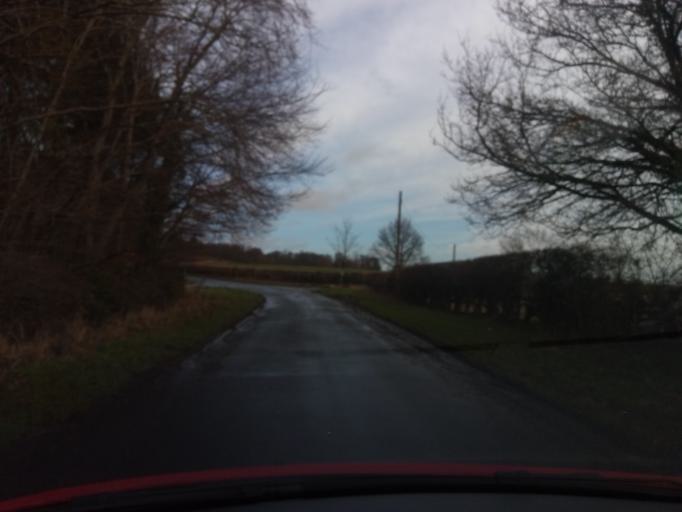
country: GB
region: England
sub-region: Northumberland
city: Corbridge
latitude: 54.9885
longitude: -2.0359
